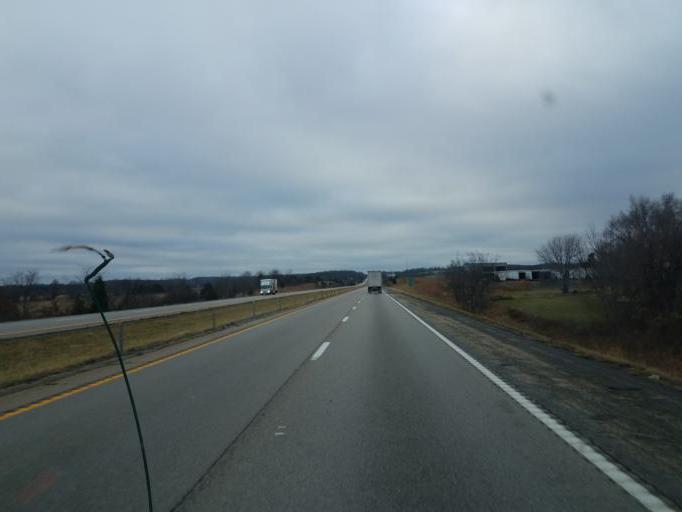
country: US
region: Missouri
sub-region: Laclede County
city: Lebanon
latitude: 37.5781
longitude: -92.7549
